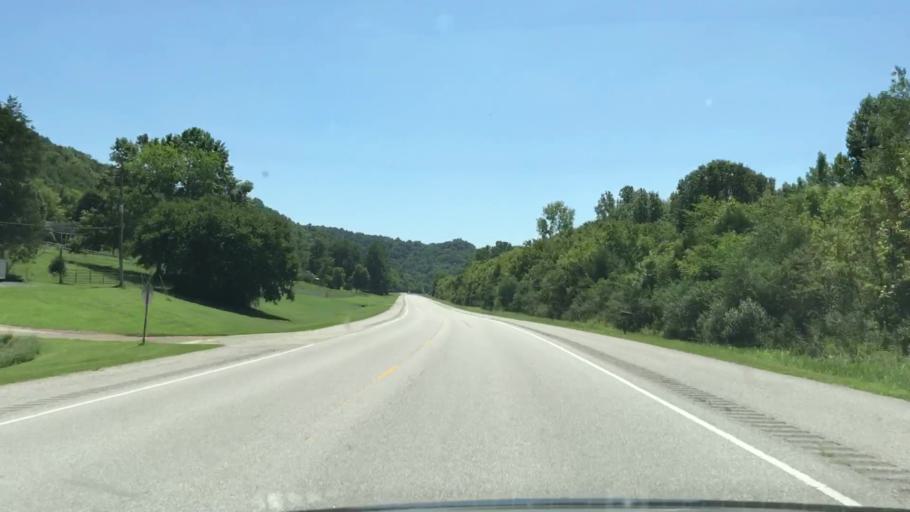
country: US
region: Tennessee
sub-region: Jackson County
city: Gainesboro
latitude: 36.4095
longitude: -85.6380
